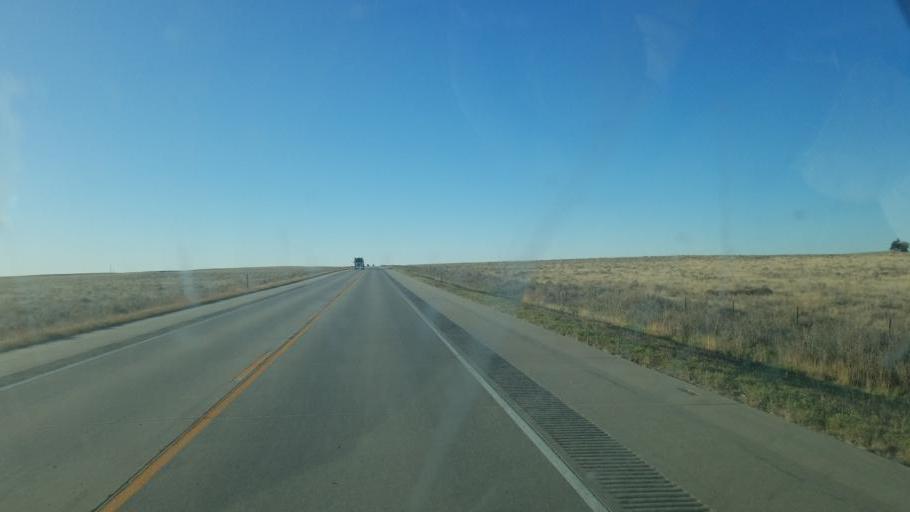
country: US
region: Colorado
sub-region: Kiowa County
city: Eads
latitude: 38.5510
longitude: -102.7861
